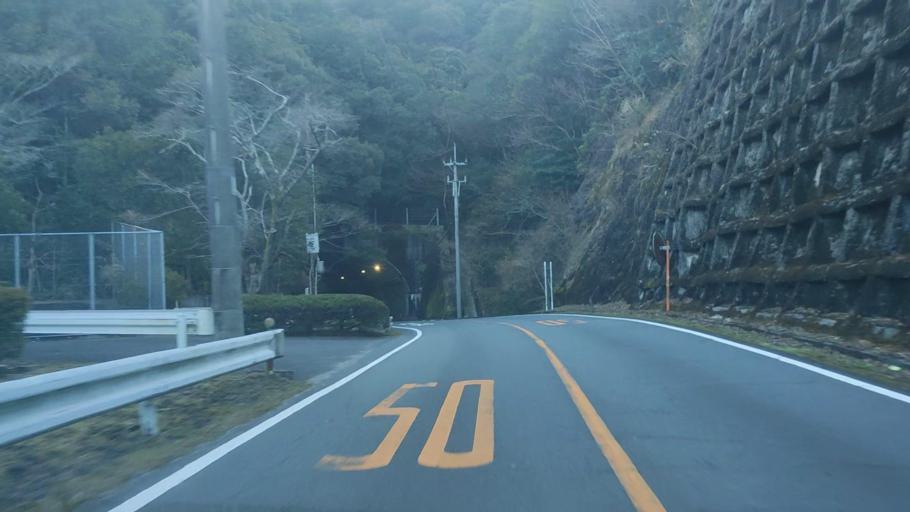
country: JP
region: Miyazaki
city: Nobeoka
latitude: 32.6320
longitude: 131.7282
